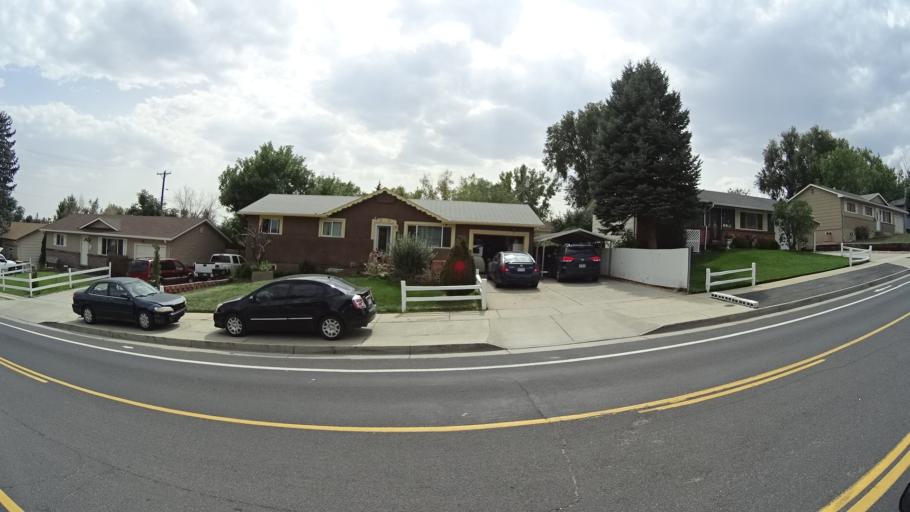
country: US
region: Colorado
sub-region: El Paso County
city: Colorado Springs
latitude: 38.8358
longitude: -104.7652
